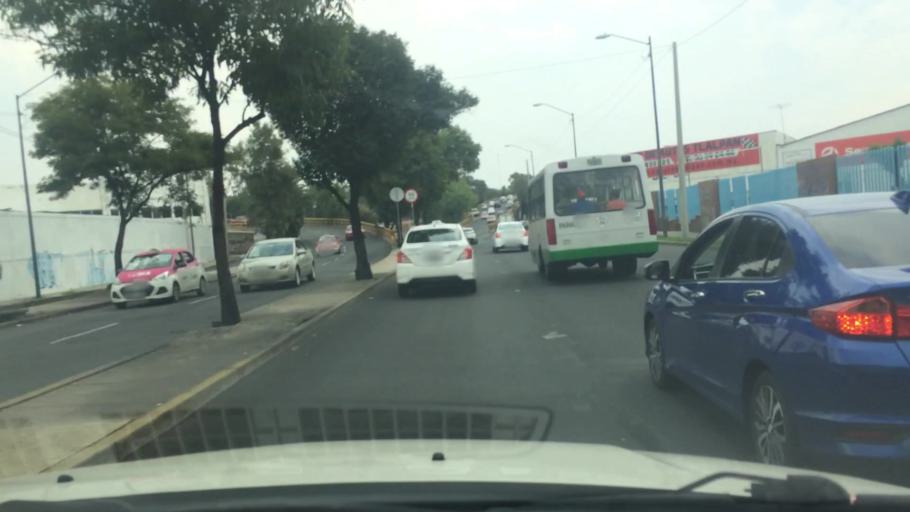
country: MX
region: Mexico City
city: Tlalpan
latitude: 19.3159
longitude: -99.1371
